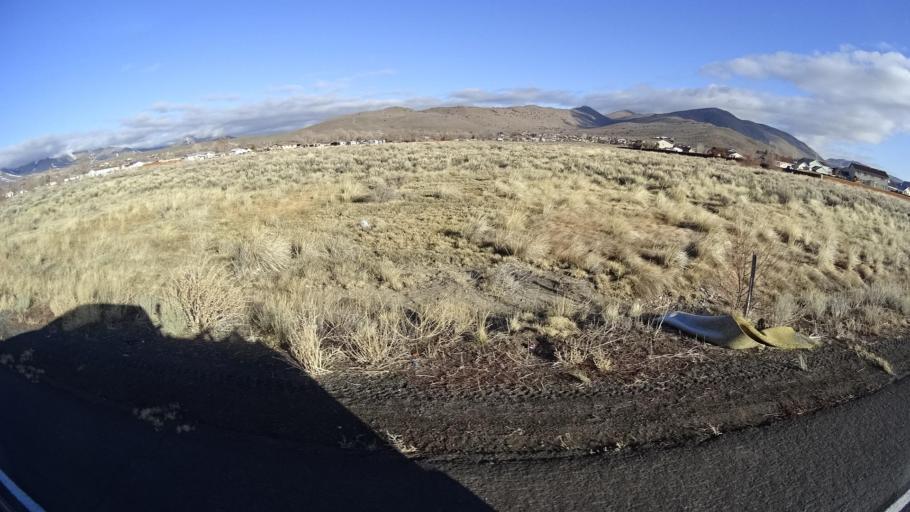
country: US
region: Nevada
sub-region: Washoe County
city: Cold Springs
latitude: 39.6729
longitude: -119.9856
